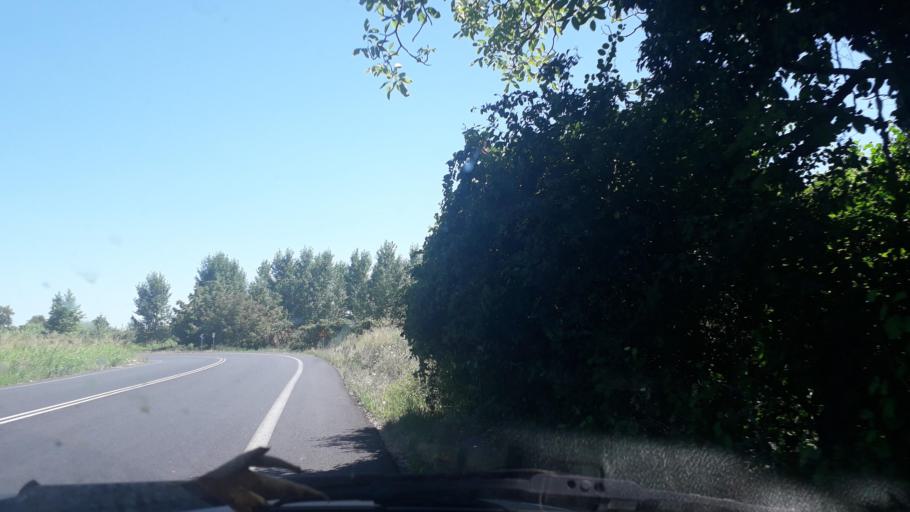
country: GR
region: Central Macedonia
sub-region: Nomos Pellis
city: Tsakoi
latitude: 40.9728
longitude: 22.0108
